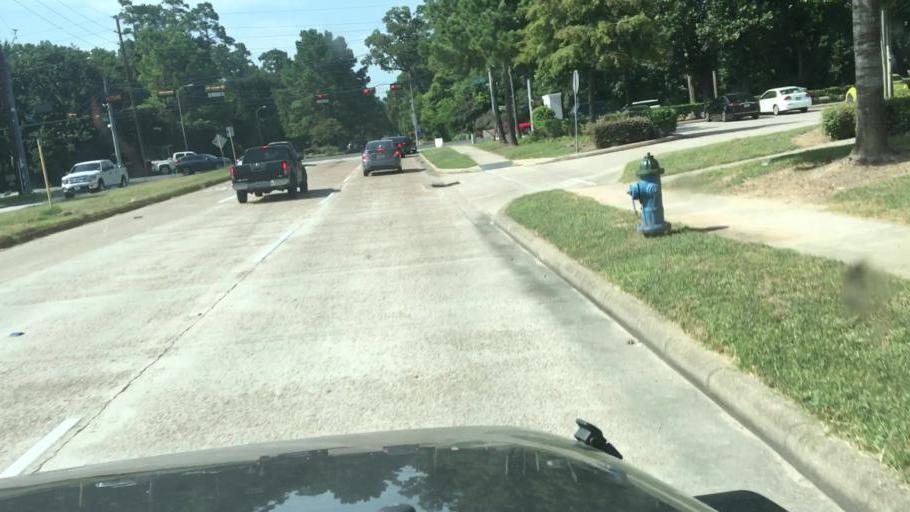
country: US
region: Texas
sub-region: Harris County
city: Atascocita
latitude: 29.9978
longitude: -95.1782
